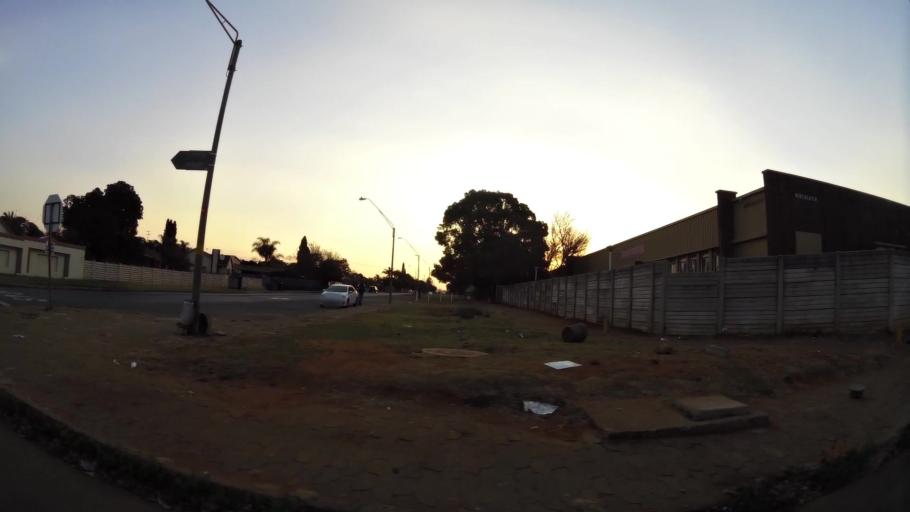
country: ZA
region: Gauteng
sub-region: Ekurhuleni Metropolitan Municipality
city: Tembisa
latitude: -26.0637
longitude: 28.2302
